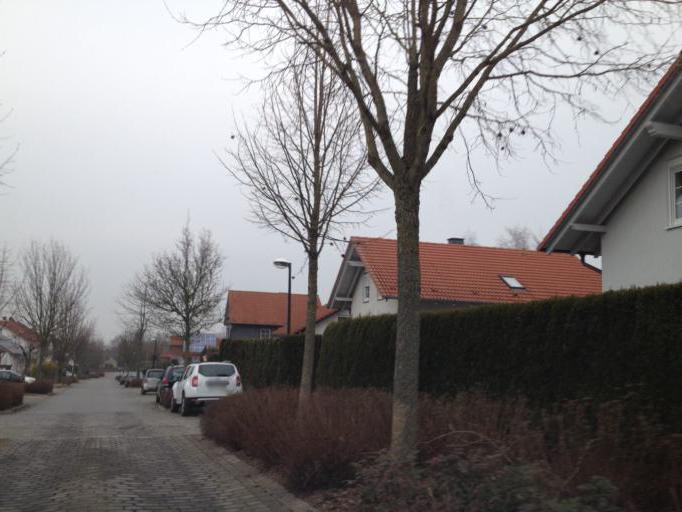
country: DE
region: North Rhine-Westphalia
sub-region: Regierungsbezirk Arnsberg
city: Mohnesee
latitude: 51.5088
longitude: 8.0908
